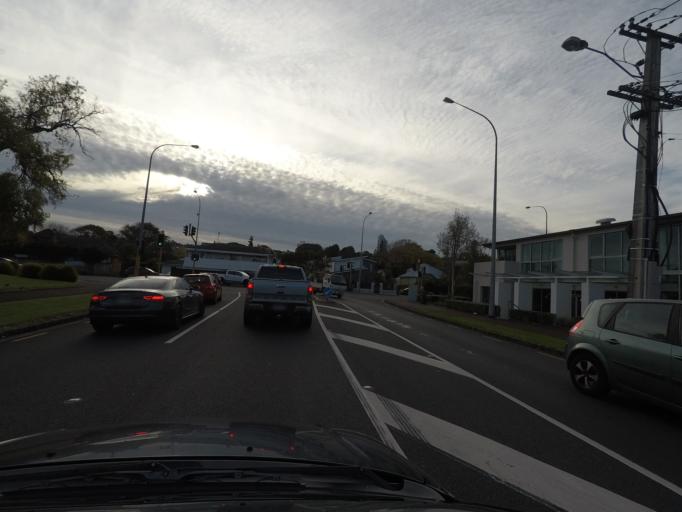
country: NZ
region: Auckland
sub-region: Auckland
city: Auckland
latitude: -36.8857
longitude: 174.8034
